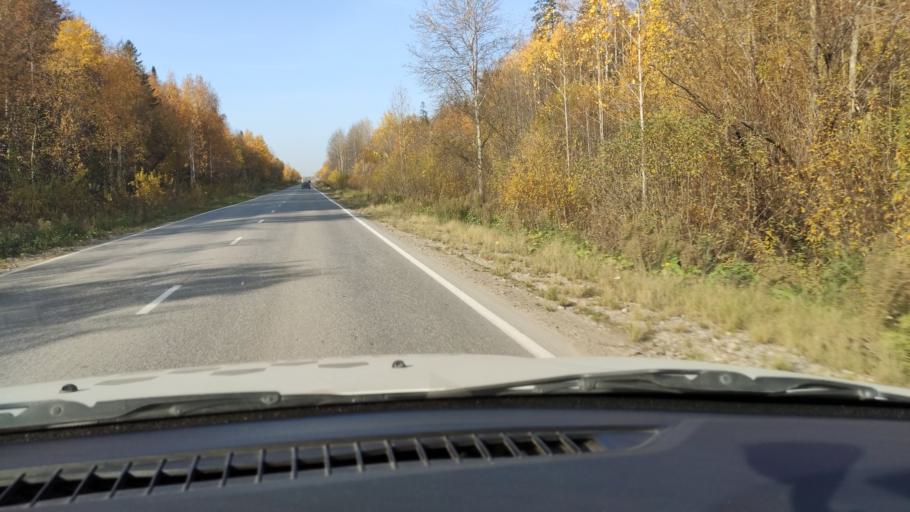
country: RU
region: Perm
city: Novyye Lyady
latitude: 58.0266
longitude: 56.6307
